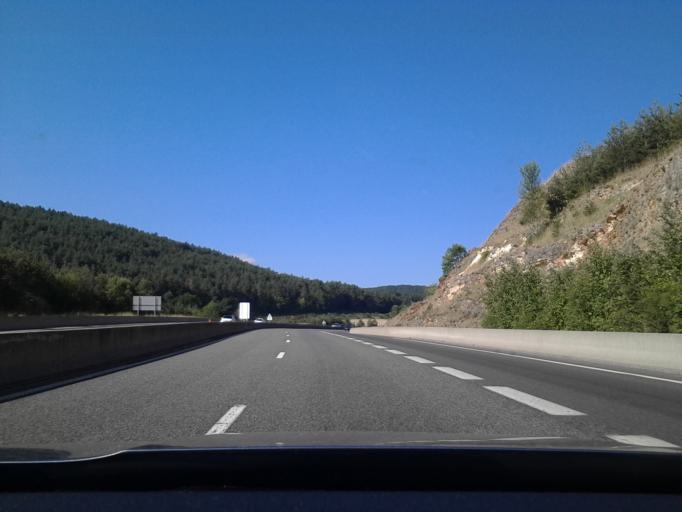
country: FR
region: Languedoc-Roussillon
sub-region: Departement de la Lozere
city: La Canourgue
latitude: 44.4047
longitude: 3.1708
